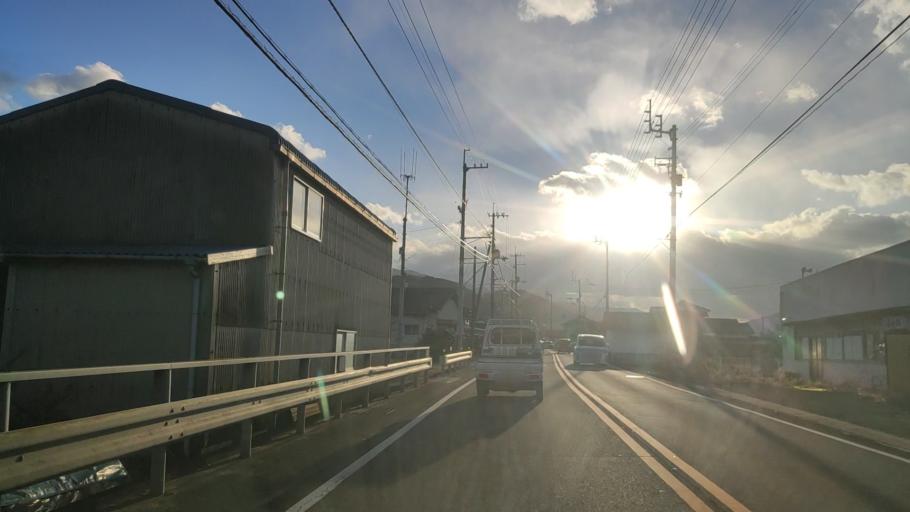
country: JP
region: Ehime
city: Saijo
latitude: 33.8885
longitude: 133.0856
